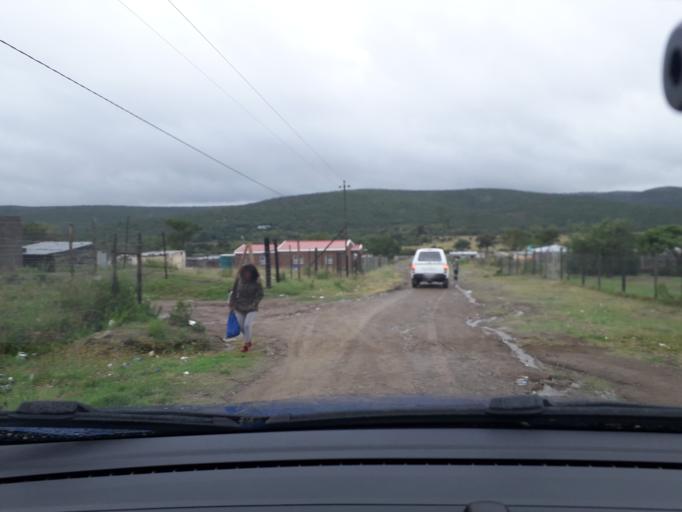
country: ZA
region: Eastern Cape
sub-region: Buffalo City Metropolitan Municipality
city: Bhisho
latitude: -32.8071
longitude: 27.3675
